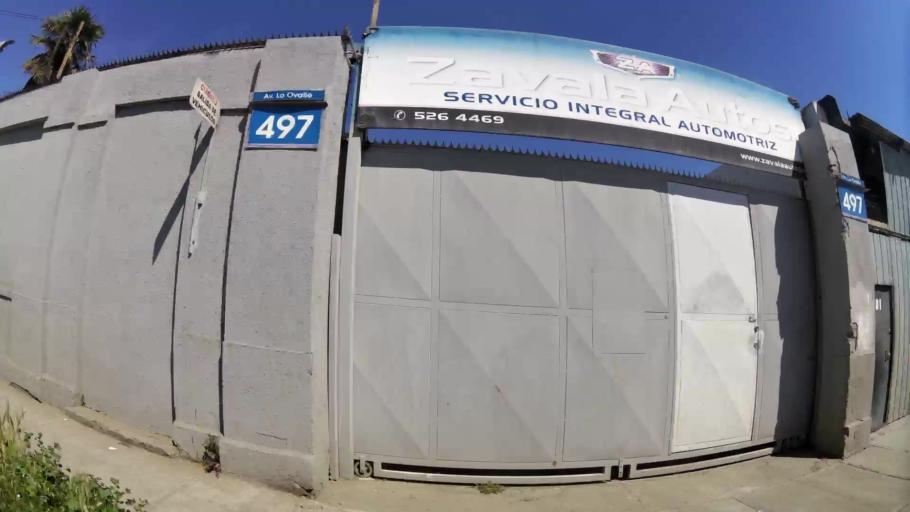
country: CL
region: Santiago Metropolitan
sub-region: Provincia de Santiago
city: Santiago
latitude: -33.5159
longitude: -70.6523
